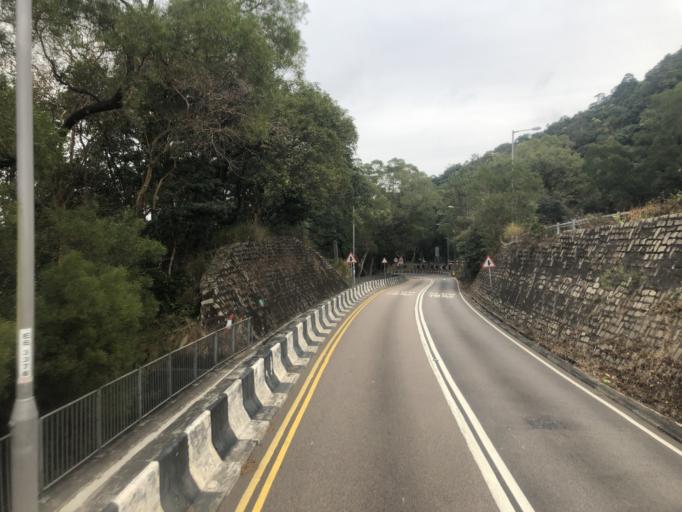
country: HK
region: Sai Kung
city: Sai Kung
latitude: 22.3435
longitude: 114.2502
